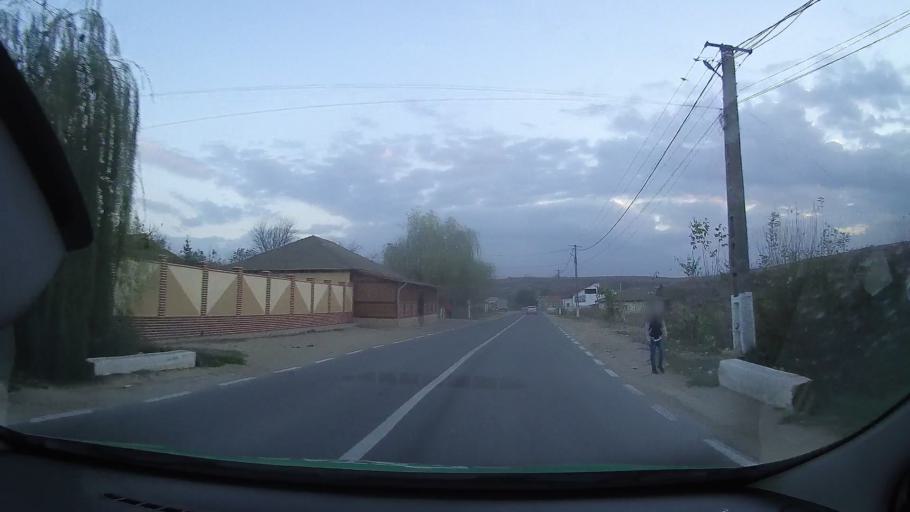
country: RO
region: Constanta
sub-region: Comuna Baneasa
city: Baneasa
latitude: 44.0744
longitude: 27.6899
